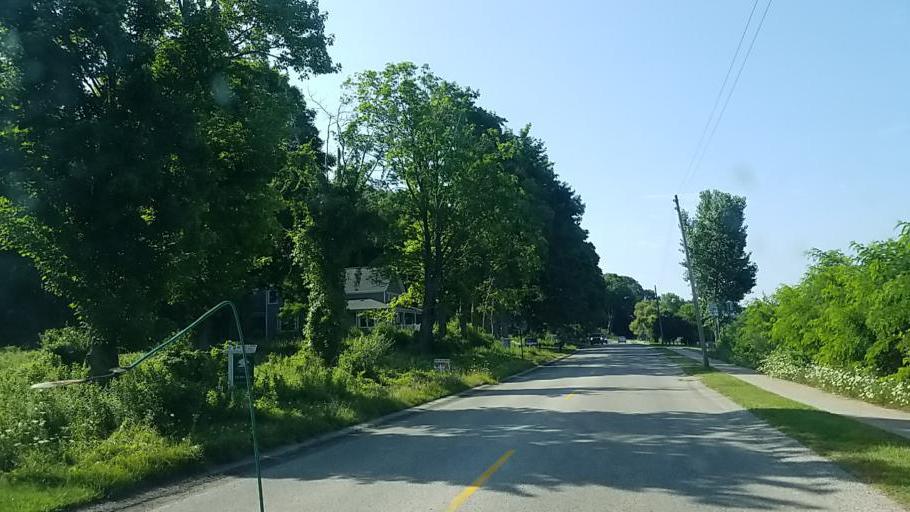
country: US
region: Michigan
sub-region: Muskegon County
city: Whitehall
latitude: 43.3944
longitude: -86.3535
